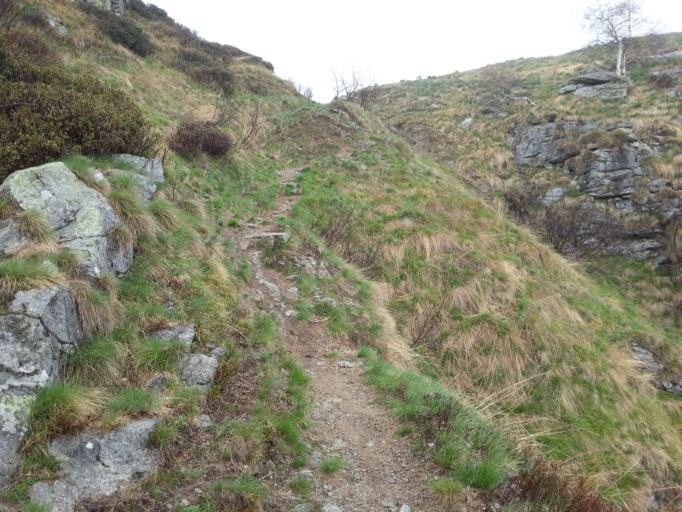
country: IT
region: Lombardy
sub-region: Provincia di Varese
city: Curiglia
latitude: 46.0550
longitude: 8.8557
